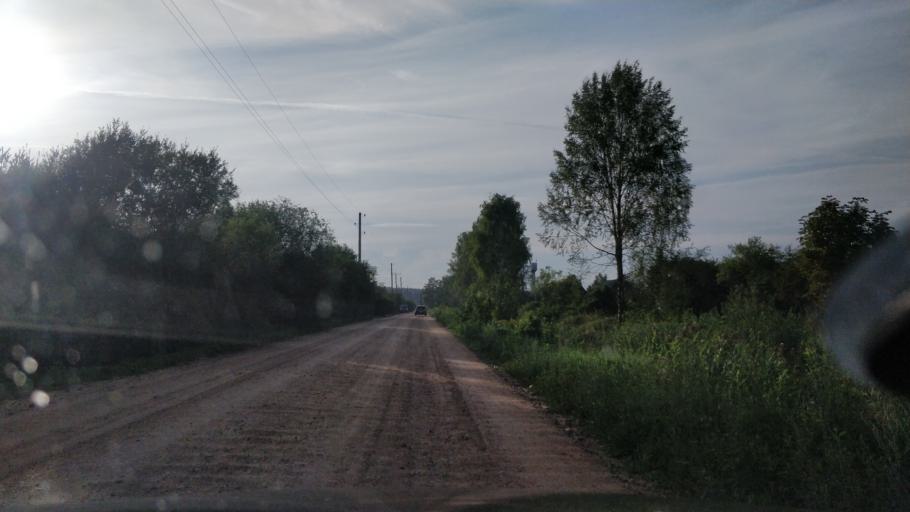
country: LV
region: Incukalns
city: Incukalns
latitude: 57.0974
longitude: 24.7565
